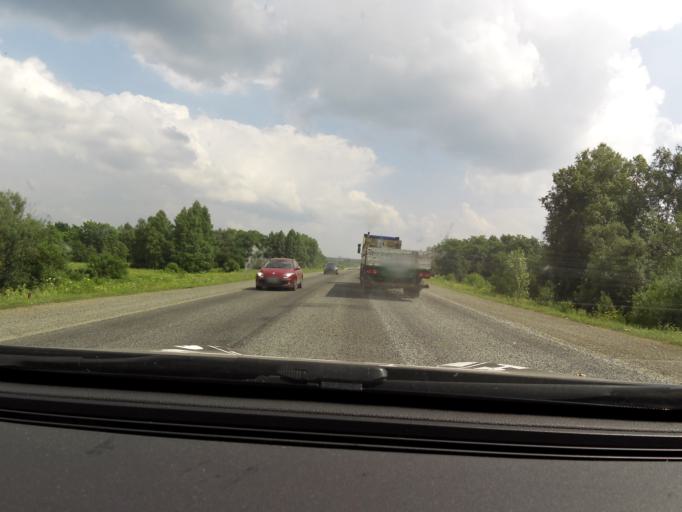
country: RU
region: Sverdlovsk
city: Ufimskiy
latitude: 56.7686
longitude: 58.1282
